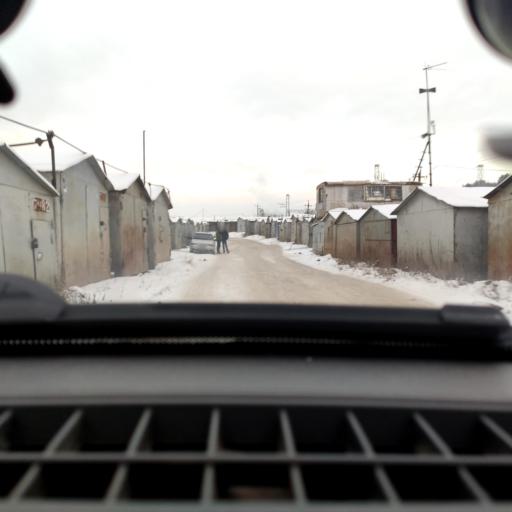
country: RU
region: Bashkortostan
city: Ufa
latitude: 54.8067
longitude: 56.1405
